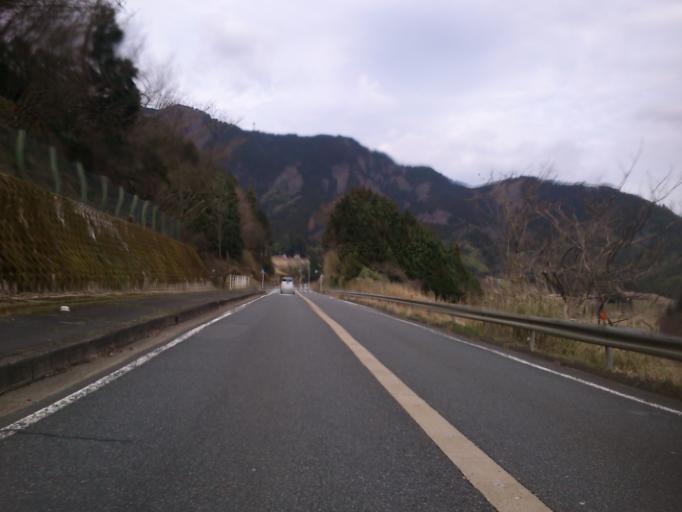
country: JP
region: Kyoto
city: Fukuchiyama
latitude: 35.3974
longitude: 135.0866
